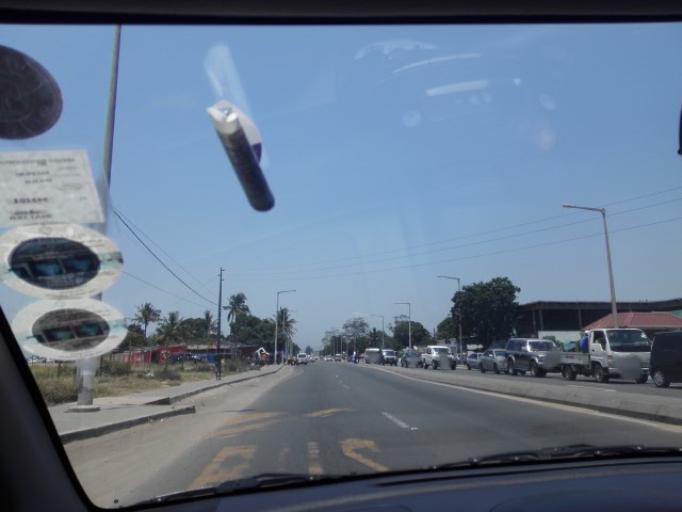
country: MZ
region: Maputo City
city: Maputo
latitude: -25.9222
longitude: 32.5618
